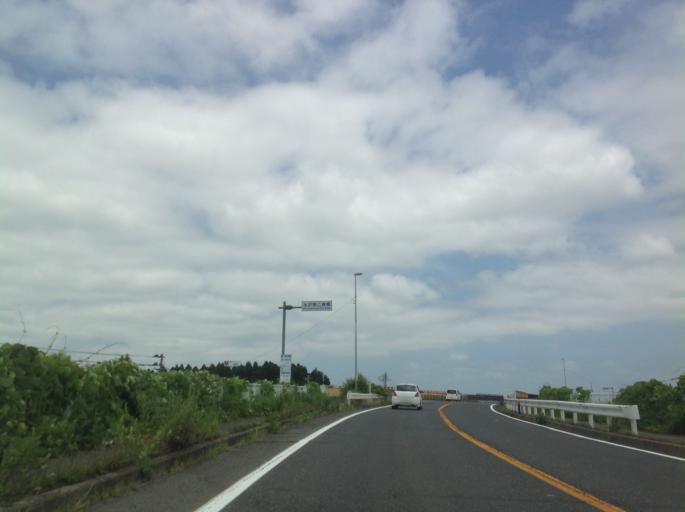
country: JP
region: Iwate
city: Mizusawa
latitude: 39.1264
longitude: 141.1460
